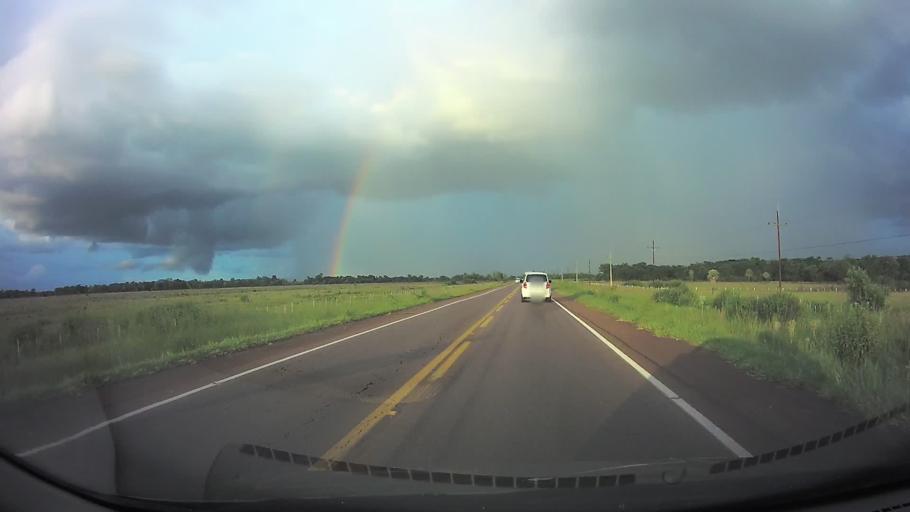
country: PY
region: Paraguari
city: Carapegua
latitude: -25.7199
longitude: -57.2002
